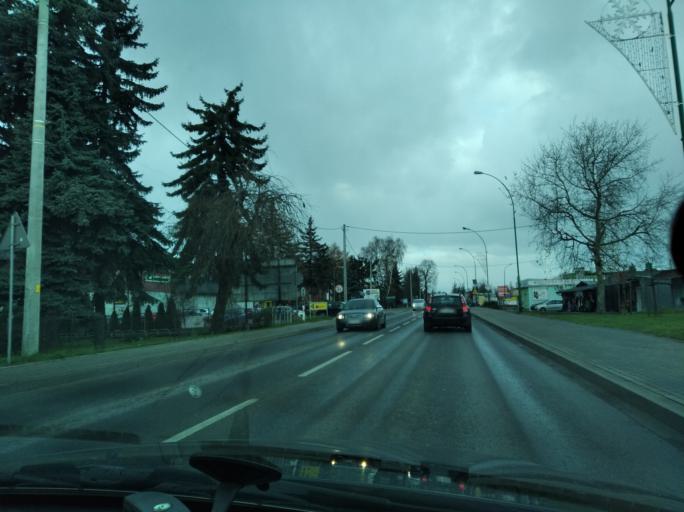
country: PL
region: Subcarpathian Voivodeship
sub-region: Powiat lancucki
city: Lancut
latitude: 50.0891
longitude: 22.2319
